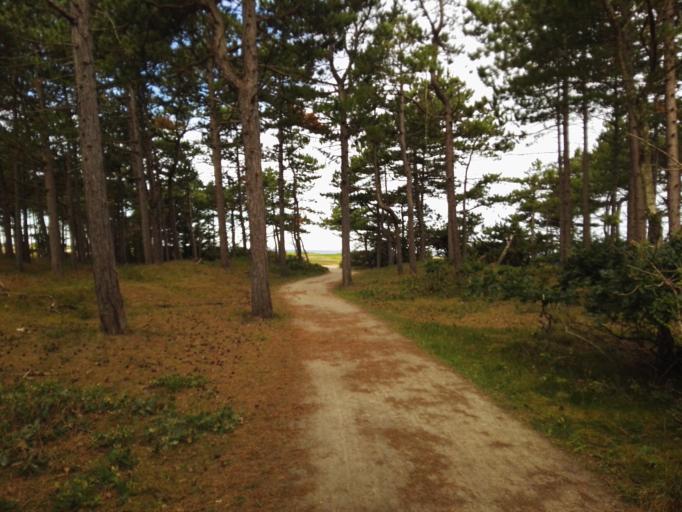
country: DK
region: Zealand
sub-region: Odsherred Kommune
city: Nykobing Sjaelland
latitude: 55.9633
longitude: 11.7402
